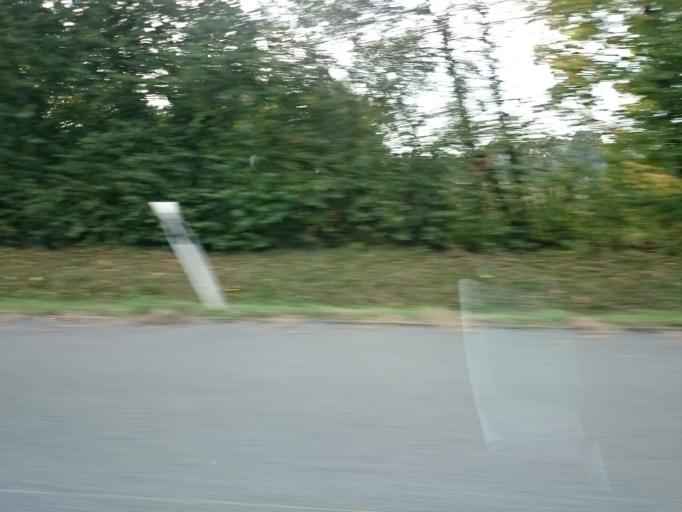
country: FR
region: Brittany
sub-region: Departement d'Ille-et-Vilaine
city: Grand-Fougeray
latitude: 47.7179
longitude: -1.7090
